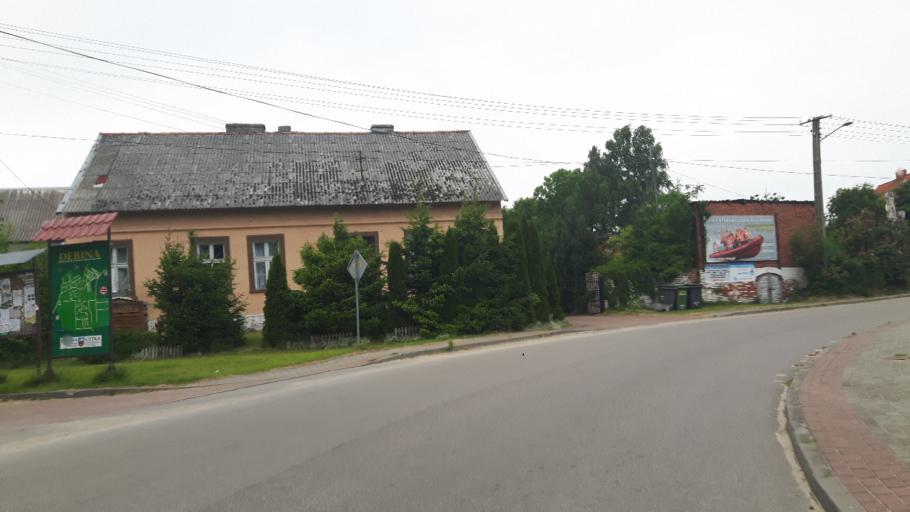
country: PL
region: Pomeranian Voivodeship
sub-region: Powiat slupski
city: Ustka
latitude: 54.6352
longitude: 17.0180
